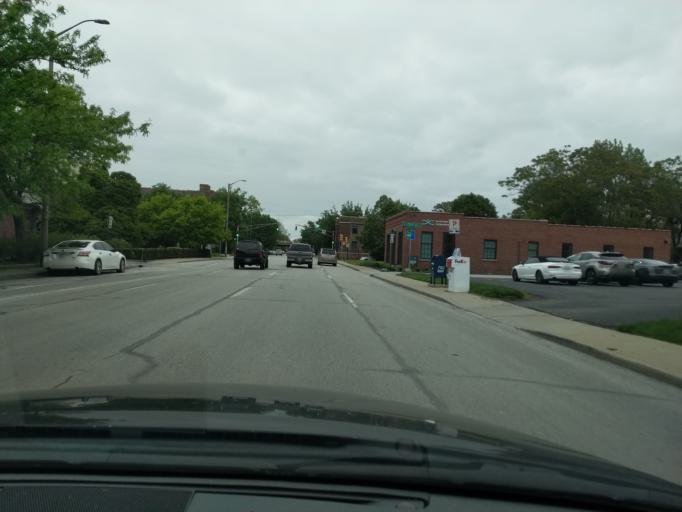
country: US
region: Indiana
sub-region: Marion County
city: Indianapolis
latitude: 39.7803
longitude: -86.1540
